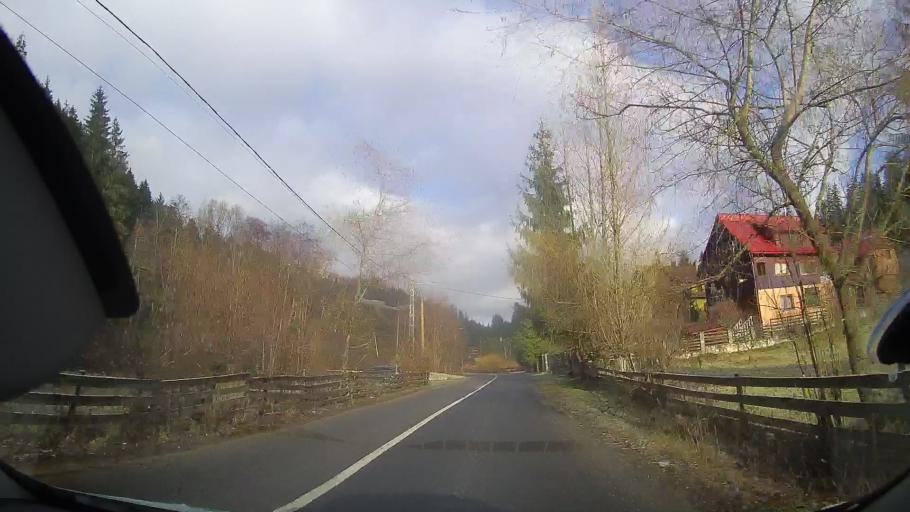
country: RO
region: Alba
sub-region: Comuna Albac
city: Albac
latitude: 46.4623
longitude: 22.9704
